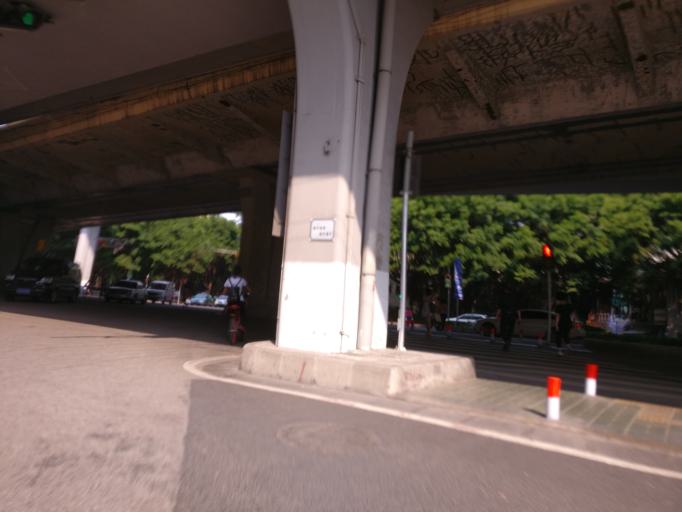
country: CN
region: Guangdong
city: Guangzhou
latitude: 23.1242
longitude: 113.2840
